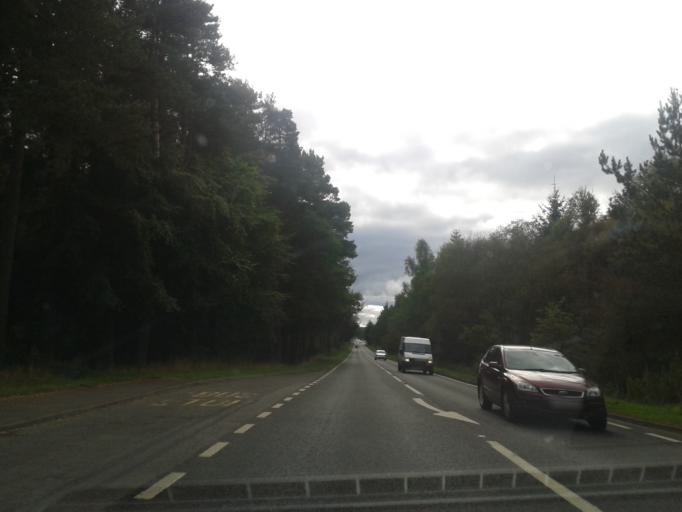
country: GB
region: Scotland
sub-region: Fife
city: Ladybank
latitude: 56.2779
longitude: -3.1352
